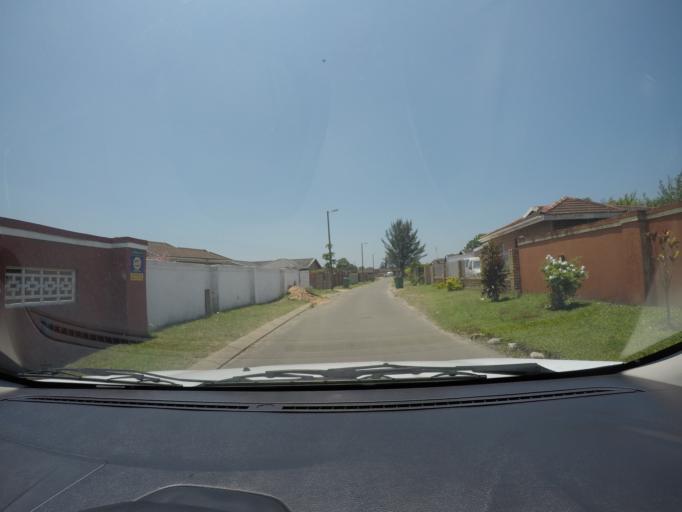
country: ZA
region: KwaZulu-Natal
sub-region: uThungulu District Municipality
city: eSikhawini
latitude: -28.8885
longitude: 31.8930
